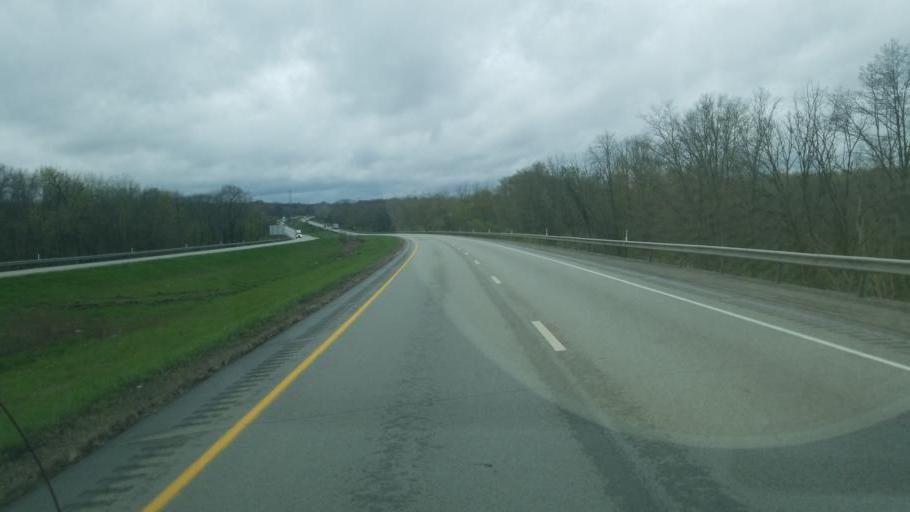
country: US
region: Pennsylvania
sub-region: Mercer County
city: Farrell
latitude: 41.1850
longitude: -80.4626
